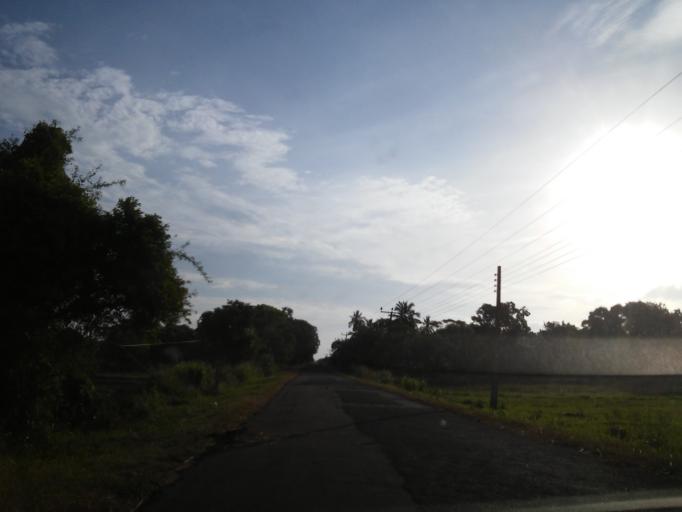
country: LK
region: Central
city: Sigiriya
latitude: 8.1675
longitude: 80.6603
